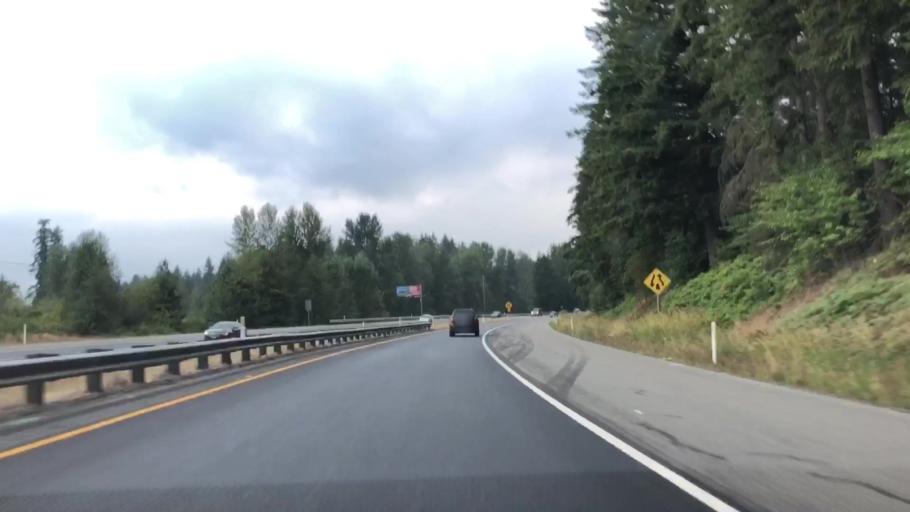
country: US
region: Washington
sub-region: Snohomish County
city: Maltby
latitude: 47.8097
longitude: -122.1059
